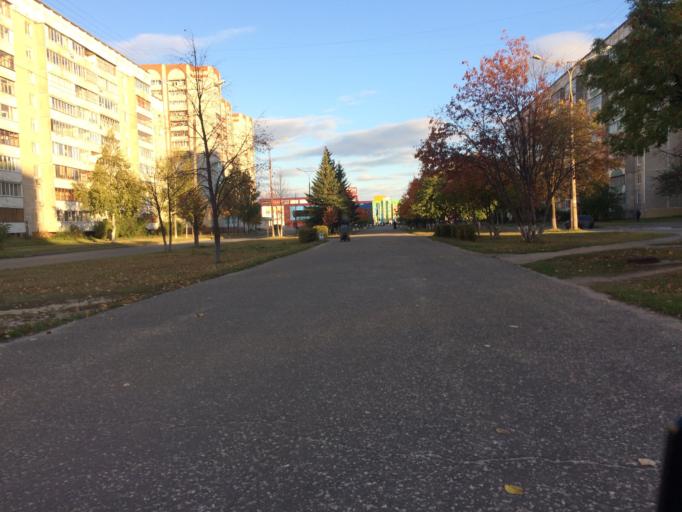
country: RU
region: Mariy-El
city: Yoshkar-Ola
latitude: 56.6296
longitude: 47.9229
